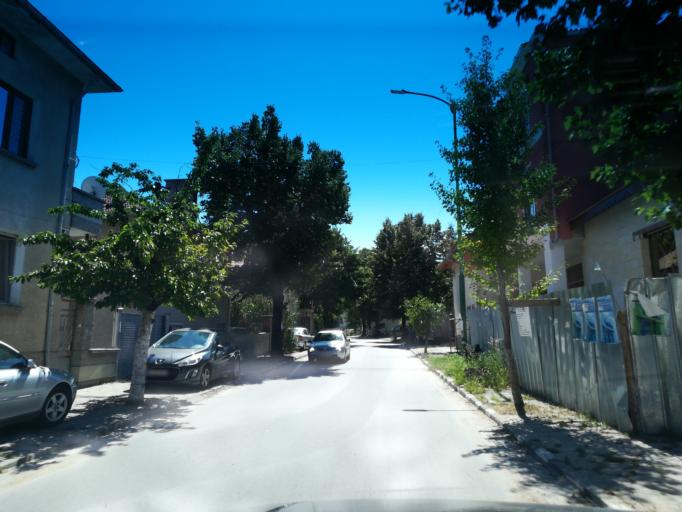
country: BG
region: Pazardzhik
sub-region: Obshtina Strelcha
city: Strelcha
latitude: 42.5089
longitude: 24.3203
